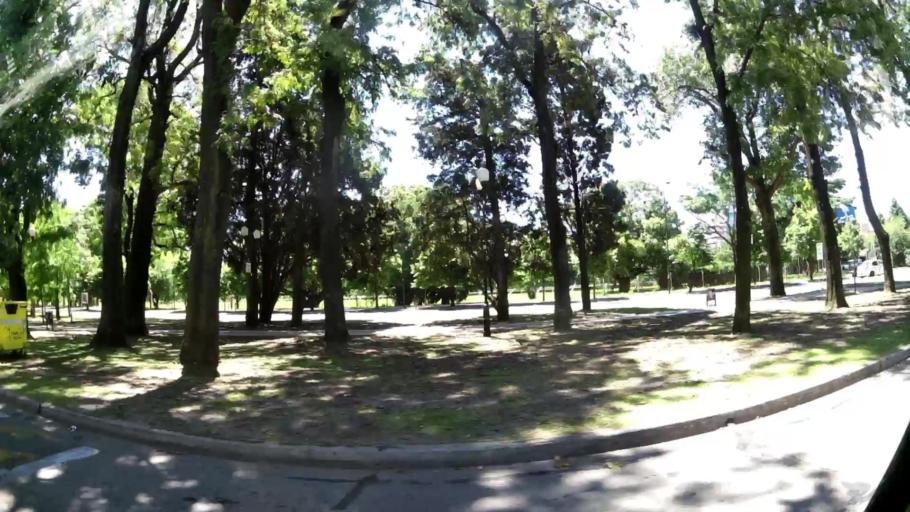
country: AR
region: Buenos Aires
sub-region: Partido de San Isidro
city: San Isidro
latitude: -34.4809
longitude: -58.5081
